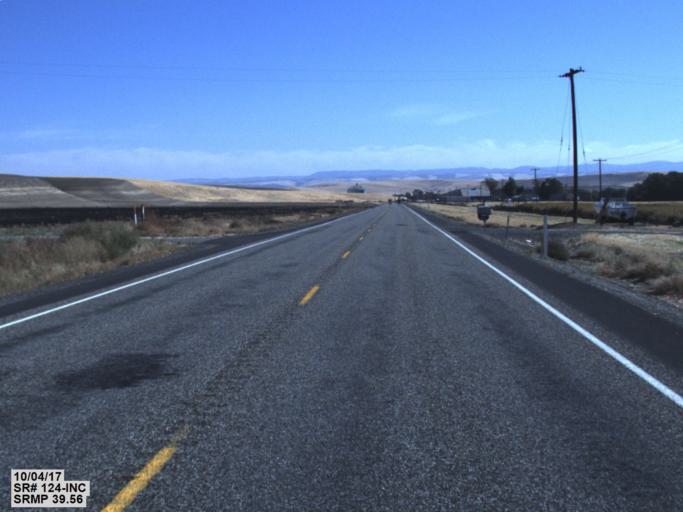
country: US
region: Washington
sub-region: Walla Walla County
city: Waitsburg
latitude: 46.2863
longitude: -118.2473
